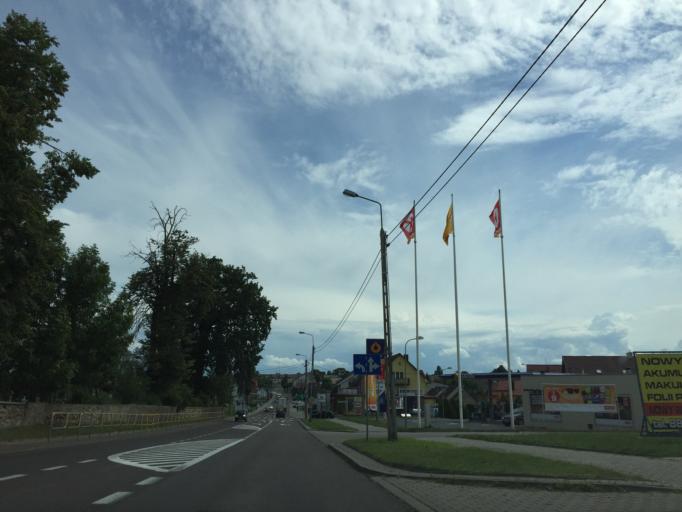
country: PL
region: Podlasie
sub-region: Powiat siemiatycki
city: Siemiatycze
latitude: 52.4325
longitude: 22.8603
